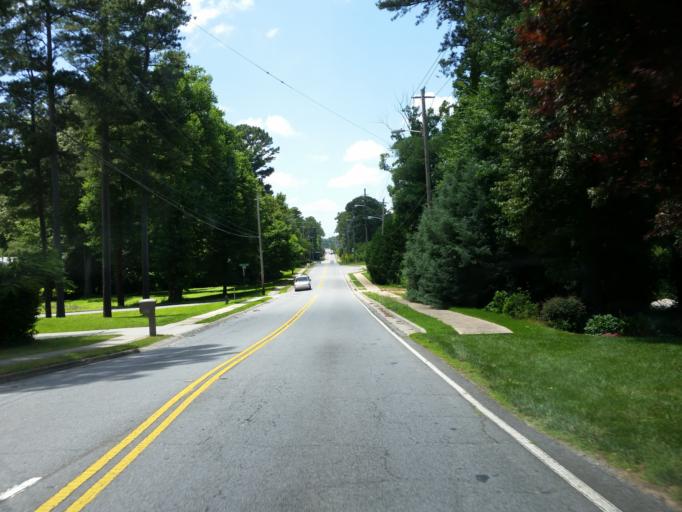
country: US
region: Georgia
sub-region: Cobb County
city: Marietta
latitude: 33.9454
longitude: -84.4828
